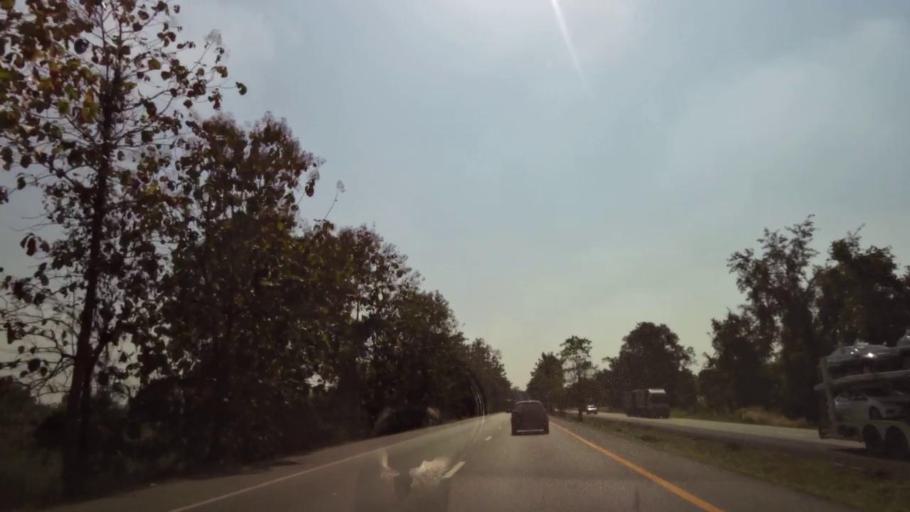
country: TH
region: Phichit
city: Bueng Na Rang
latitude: 16.0541
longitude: 100.1216
